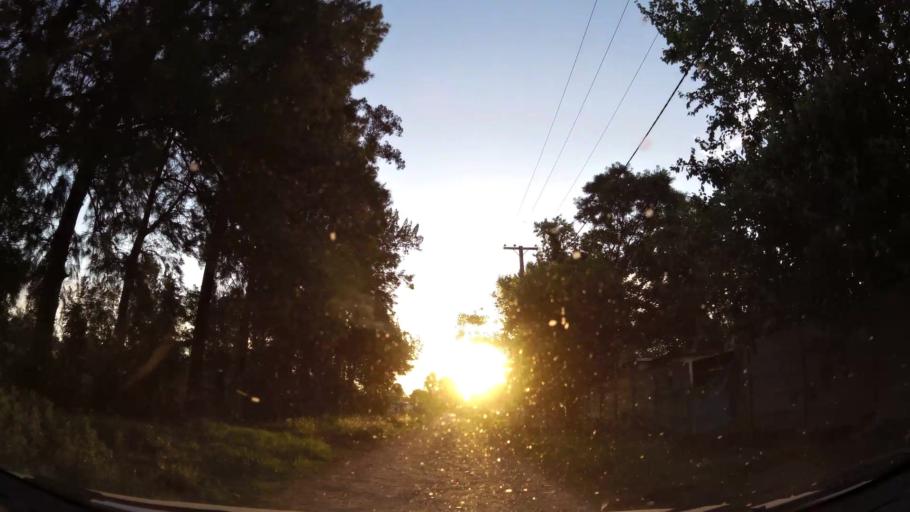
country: AR
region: Buenos Aires
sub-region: Partido de Merlo
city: Merlo
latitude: -34.6699
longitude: -58.7827
